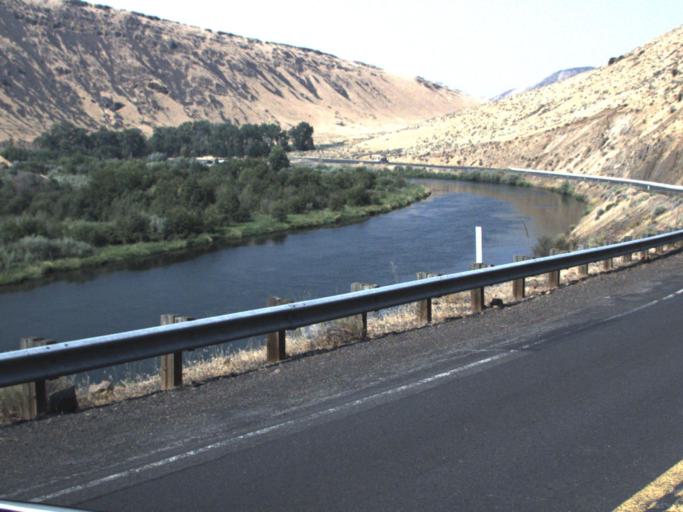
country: US
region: Washington
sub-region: Yakima County
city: Selah
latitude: 46.7582
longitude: -120.4533
